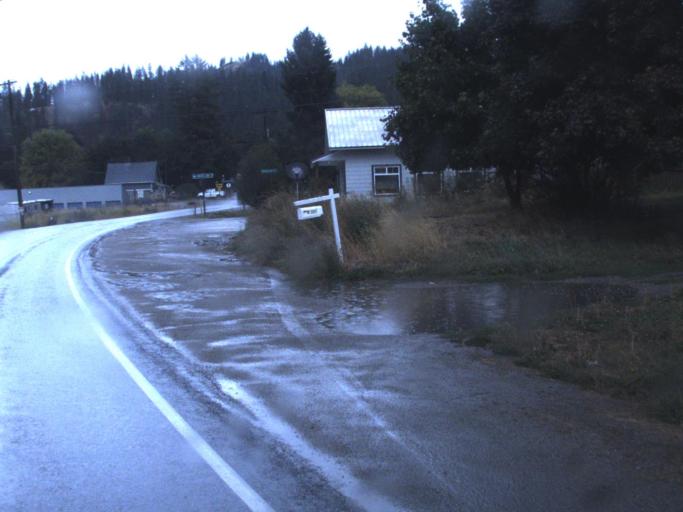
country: US
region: Washington
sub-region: Stevens County
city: Chewelah
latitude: 48.1748
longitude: -117.7248
